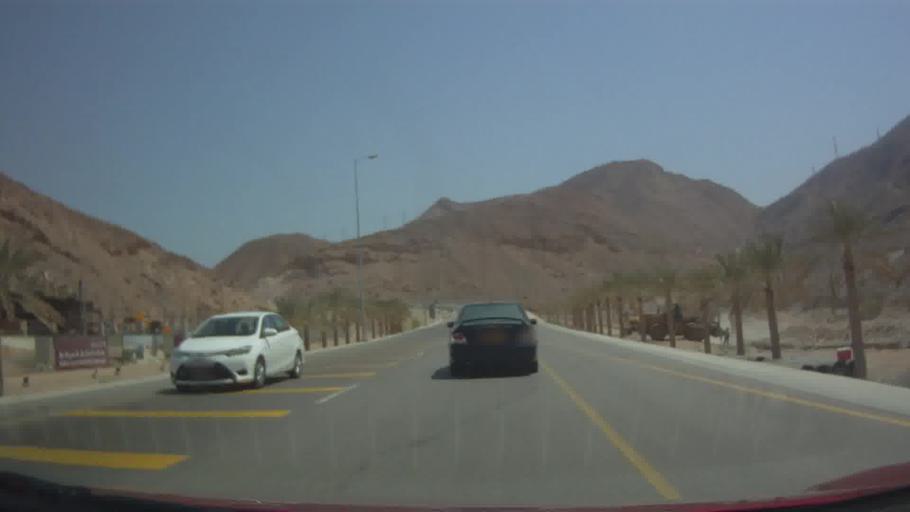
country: OM
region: Muhafazat Masqat
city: Muscat
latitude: 23.5408
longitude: 58.6324
